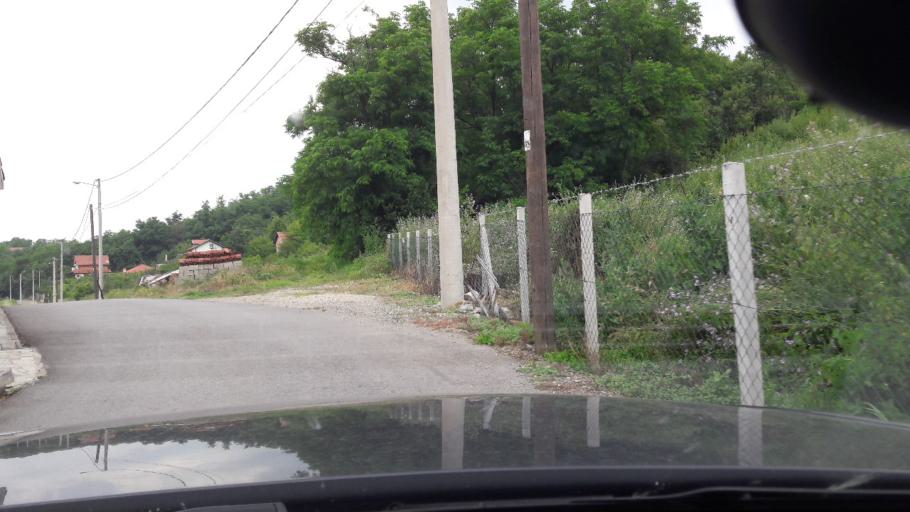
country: RS
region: Central Serbia
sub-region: Belgrade
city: Sopot
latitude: 44.6415
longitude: 20.5933
